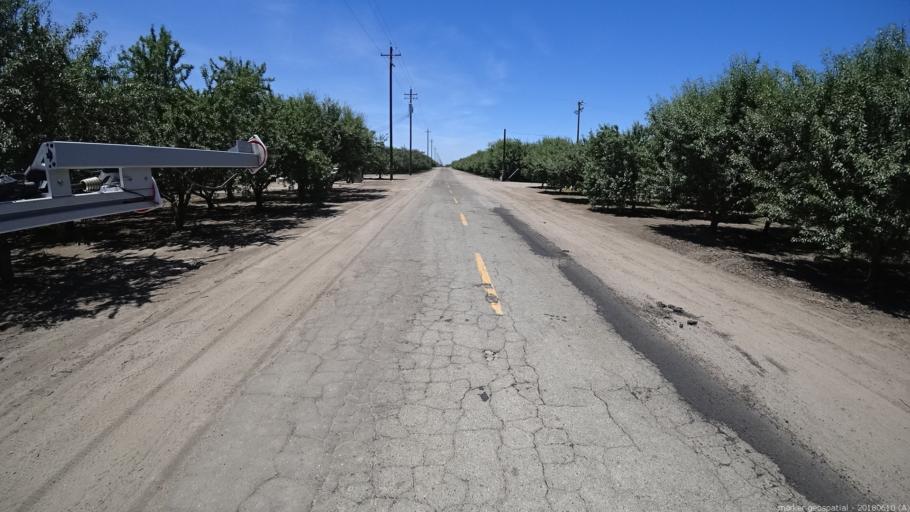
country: US
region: California
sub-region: Madera County
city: Chowchilla
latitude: 37.0545
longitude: -120.2809
